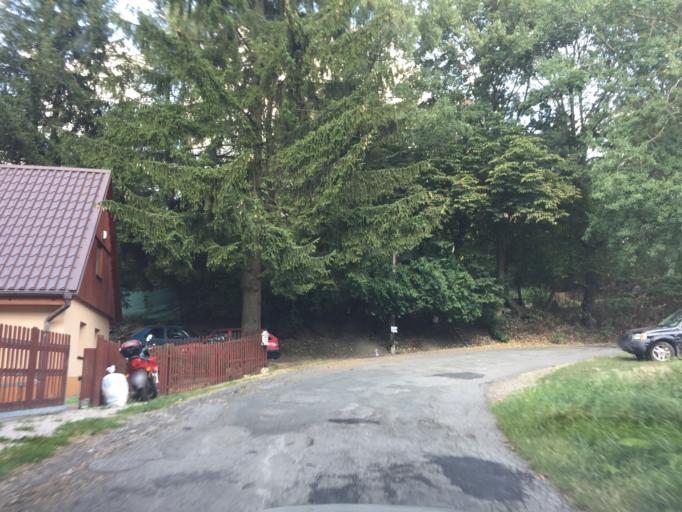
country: CZ
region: Liberecky
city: Mala Skala
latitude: 50.6710
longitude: 15.1734
